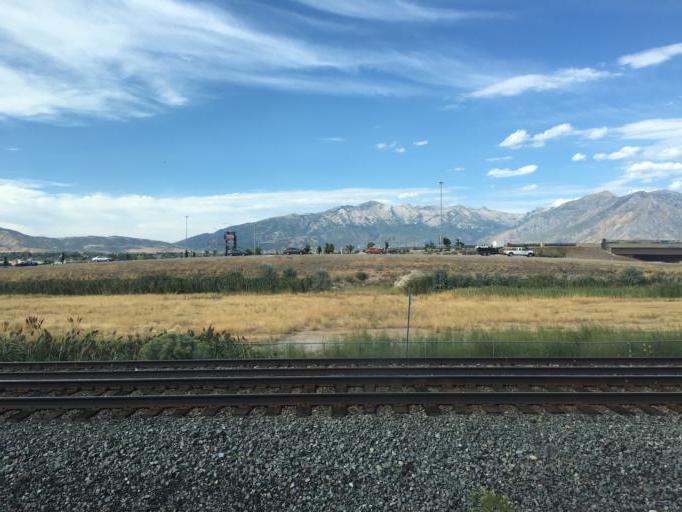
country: US
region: Utah
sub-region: Utah County
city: American Fork
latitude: 40.3748
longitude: -111.8208
